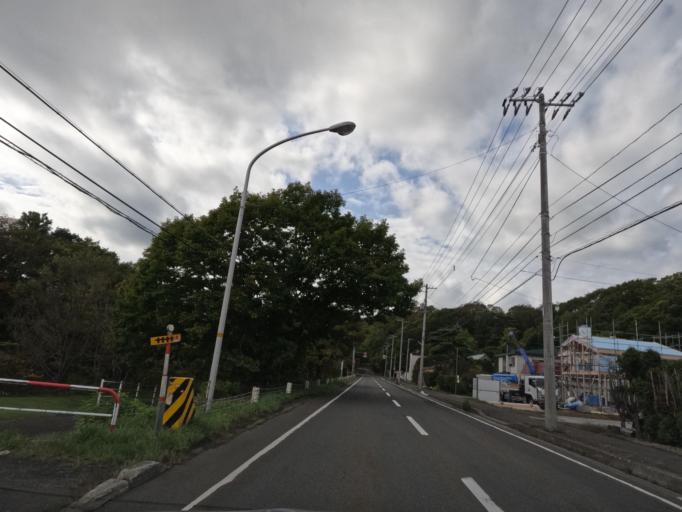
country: JP
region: Hokkaido
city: Chitose
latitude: 42.8174
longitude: 141.6149
